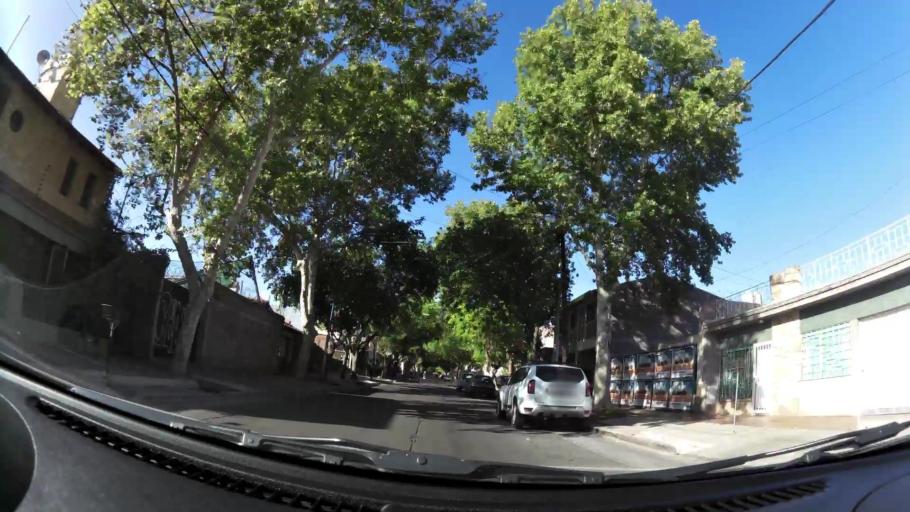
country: AR
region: Mendoza
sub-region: Departamento de Godoy Cruz
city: Godoy Cruz
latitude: -32.9299
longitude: -68.8465
